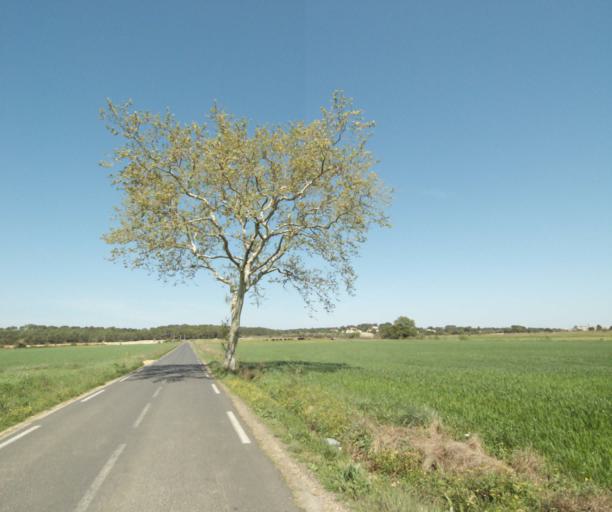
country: FR
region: Languedoc-Roussillon
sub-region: Departement de l'Herault
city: Saint-Bres
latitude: 43.6827
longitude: 4.0217
